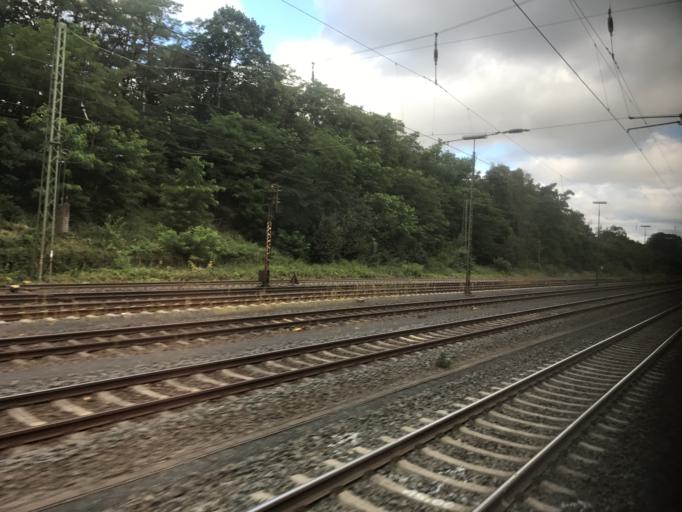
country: DE
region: Hesse
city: Allendorf an der Lahn
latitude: 50.5521
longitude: 8.6556
